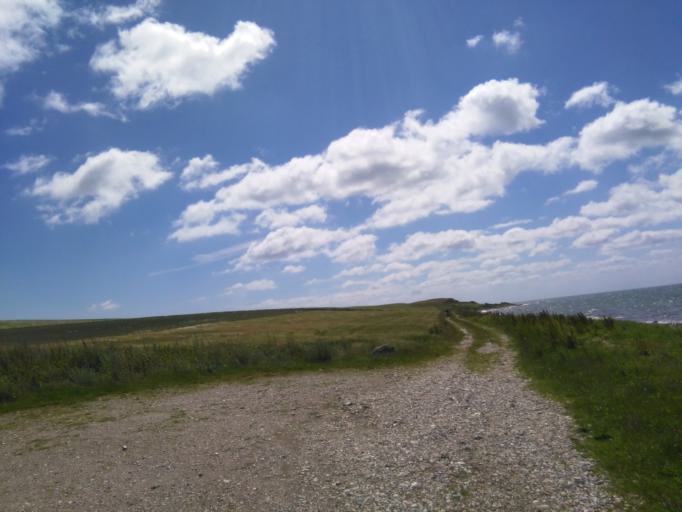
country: DK
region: Central Jutland
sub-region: Arhus Kommune
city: Logten
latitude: 56.1734
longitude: 10.3784
